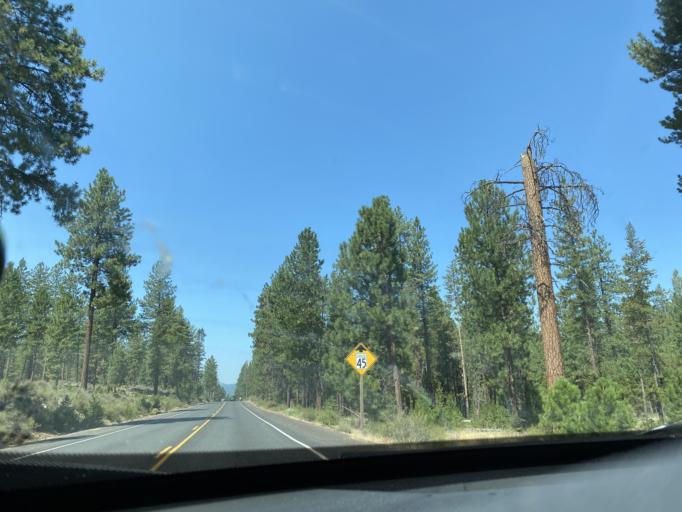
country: US
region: Oregon
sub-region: Deschutes County
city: Sunriver
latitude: 43.8915
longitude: -121.4062
